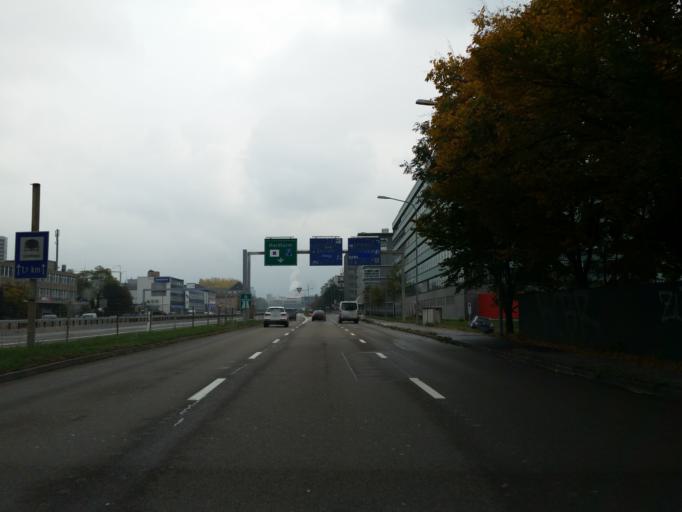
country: CH
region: Zurich
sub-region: Bezirk Zuerich
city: Zuerich (Kreis 9) / Altstetten
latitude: 47.3958
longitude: 8.4821
